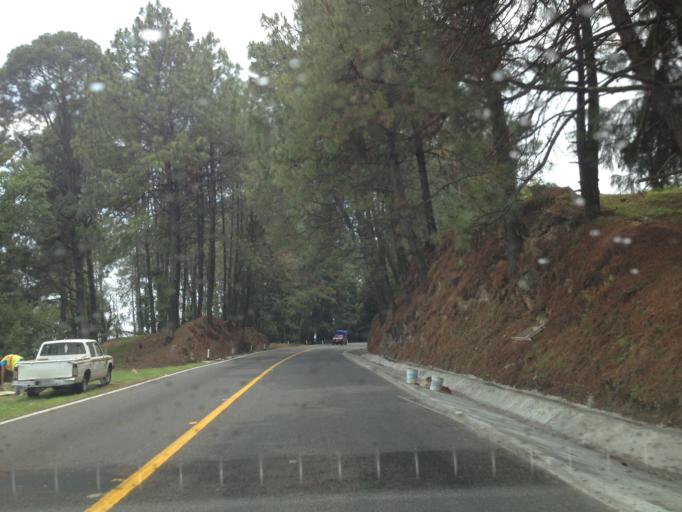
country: MX
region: Michoacan
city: Tingambato
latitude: 19.4911
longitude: -101.8773
